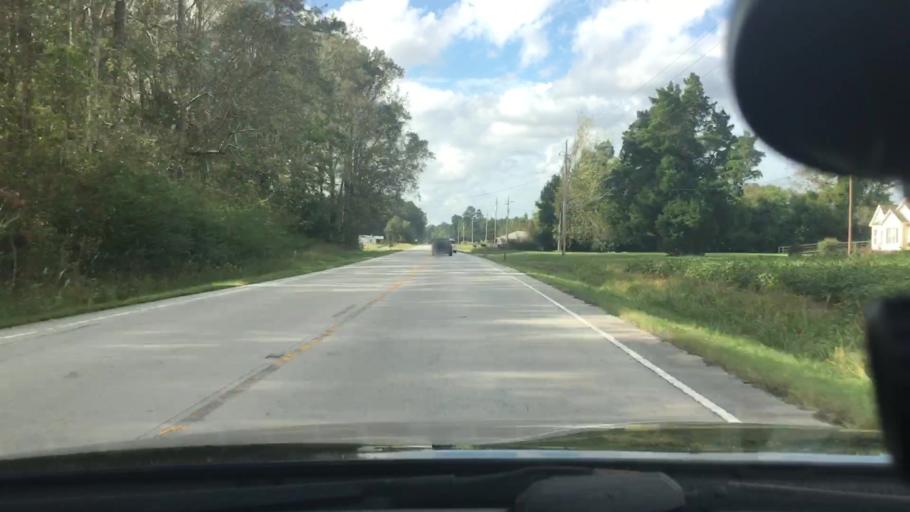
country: US
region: North Carolina
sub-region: Craven County
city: Vanceboro
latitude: 35.3995
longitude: -77.2371
